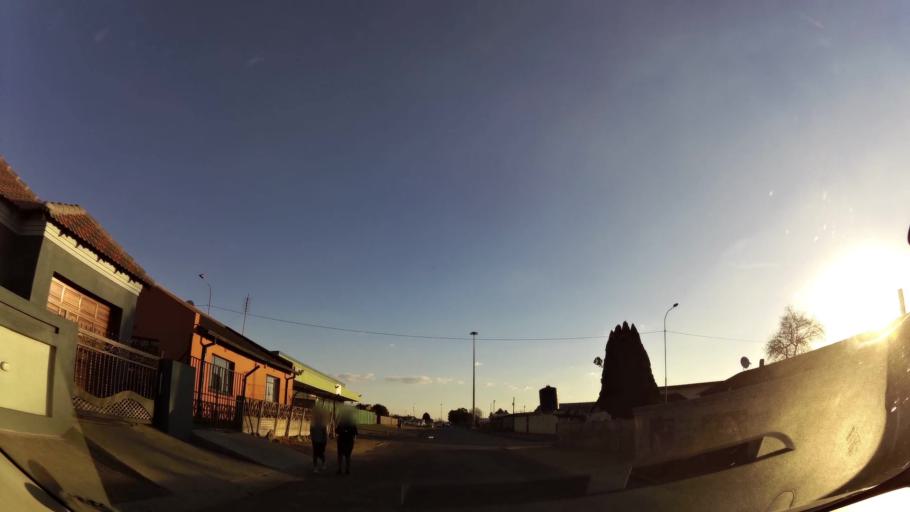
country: ZA
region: Mpumalanga
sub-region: Nkangala District Municipality
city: Witbank
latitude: -25.8786
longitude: 29.1928
